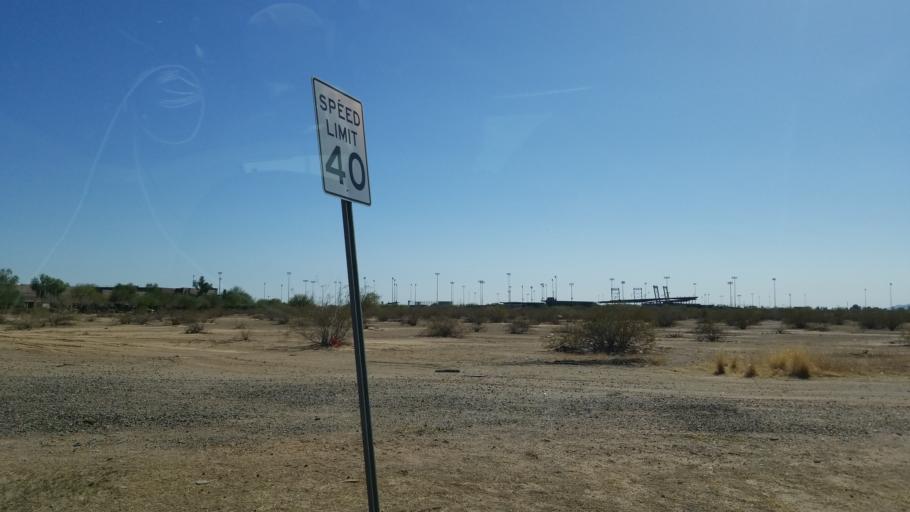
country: US
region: Arizona
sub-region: Maricopa County
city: Scottsdale
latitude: 33.5535
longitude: -111.8839
